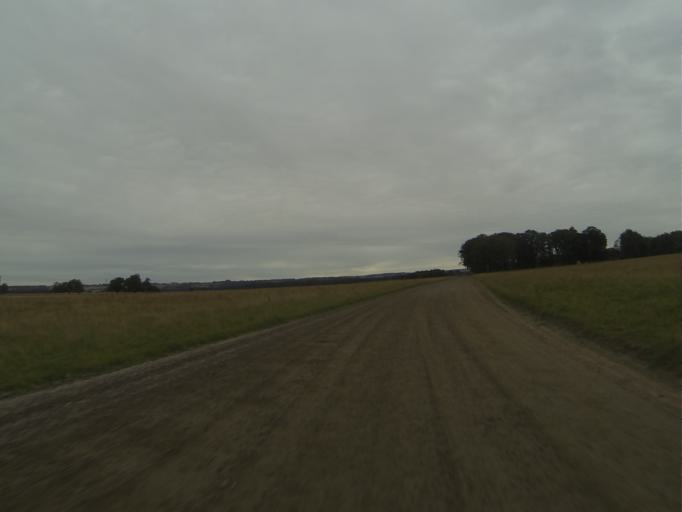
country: SE
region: Skane
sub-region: Lunds Kommun
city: Veberod
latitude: 55.7075
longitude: 13.4411
